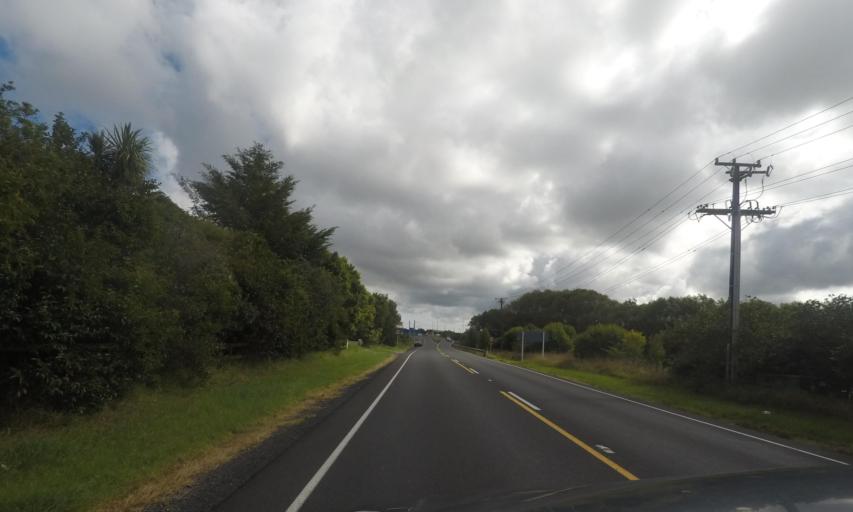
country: NZ
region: Auckland
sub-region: Auckland
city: Rosebank
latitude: -36.7958
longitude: 174.6005
